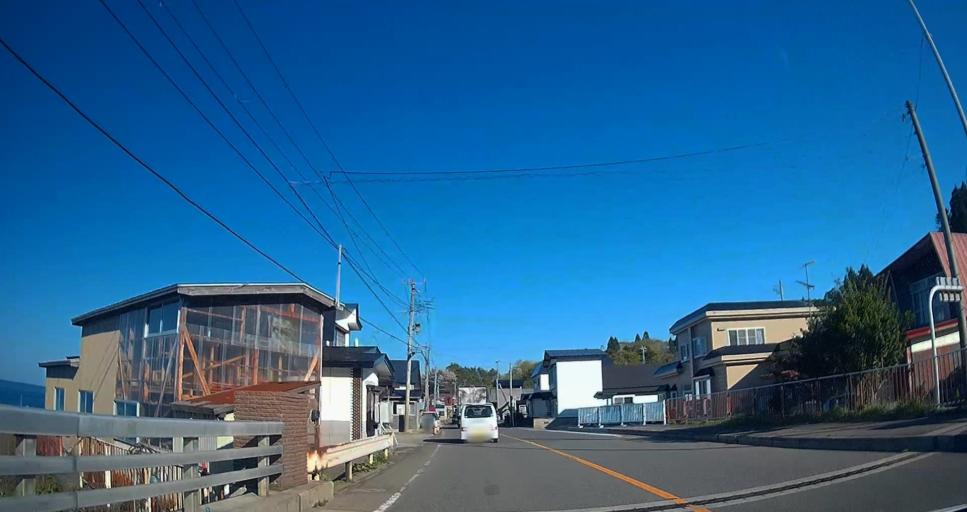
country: JP
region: Aomori
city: Mutsu
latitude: 41.4554
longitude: 141.1155
